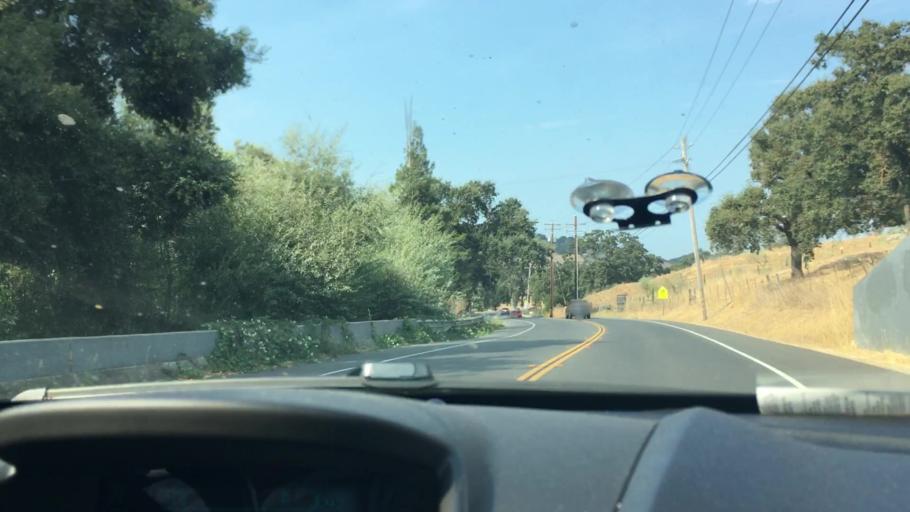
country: US
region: California
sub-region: Sonoma County
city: Petaluma
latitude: 38.1795
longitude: -122.6696
